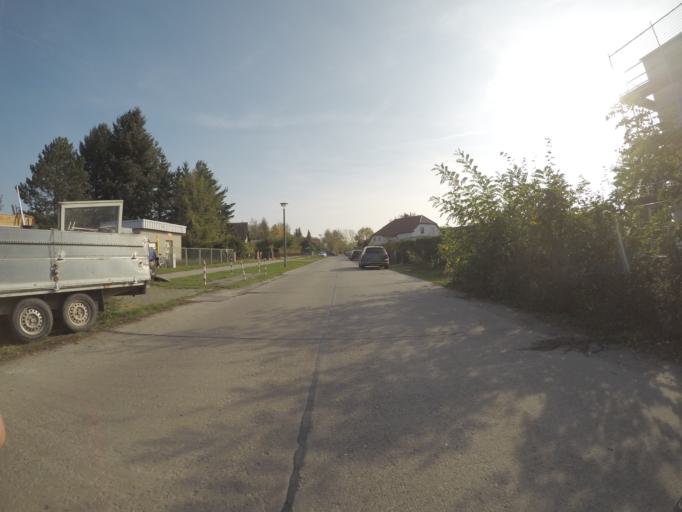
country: DE
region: Berlin
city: Altglienicke
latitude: 52.4115
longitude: 13.5466
